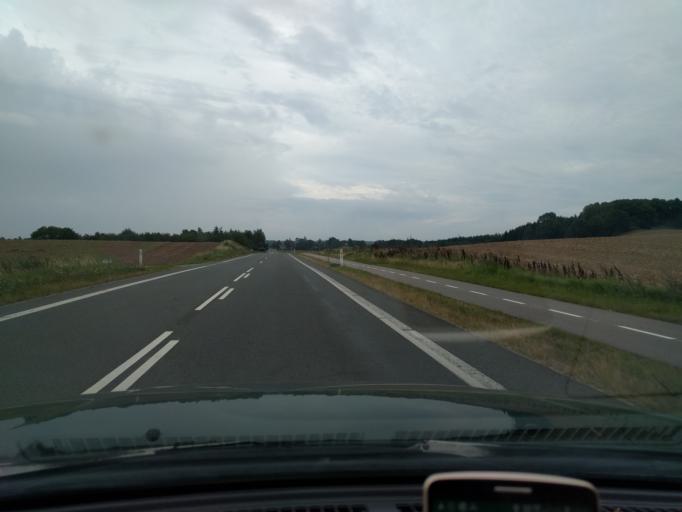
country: DK
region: Zealand
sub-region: Naestved Kommune
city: Fuglebjerg
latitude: 55.2374
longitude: 11.4341
